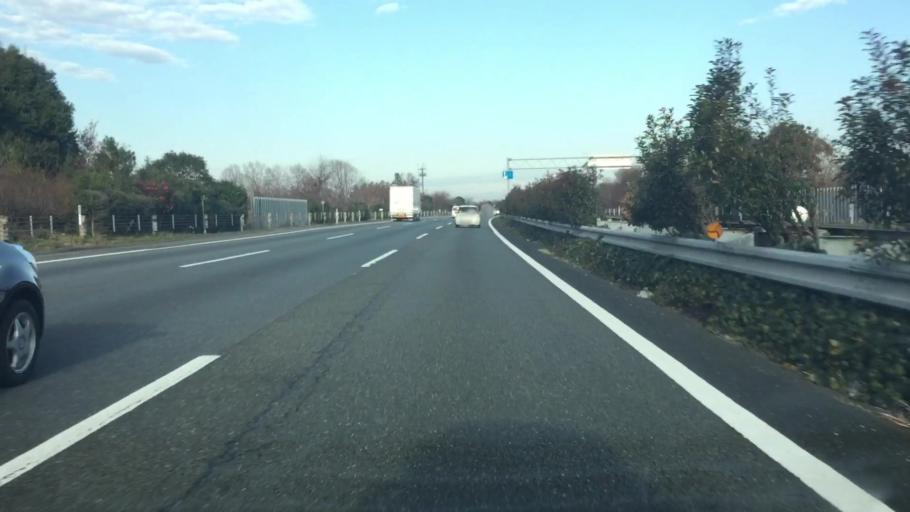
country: JP
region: Saitama
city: Yorii
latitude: 36.1359
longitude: 139.2296
